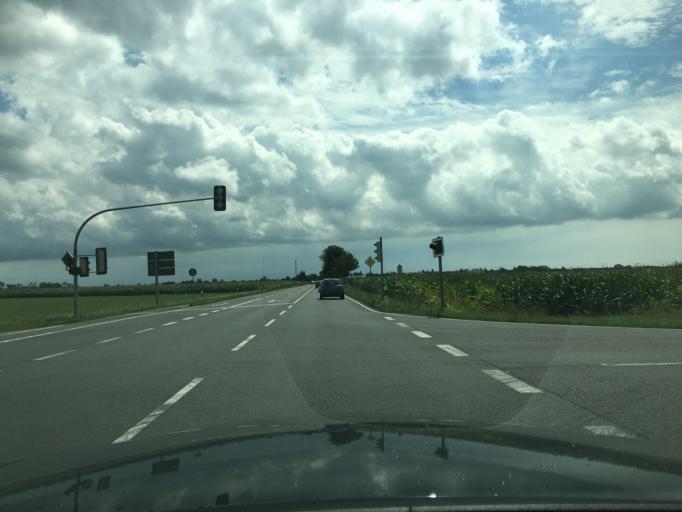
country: DE
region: Saxony-Anhalt
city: Raguhn
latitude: 51.7050
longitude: 12.2537
